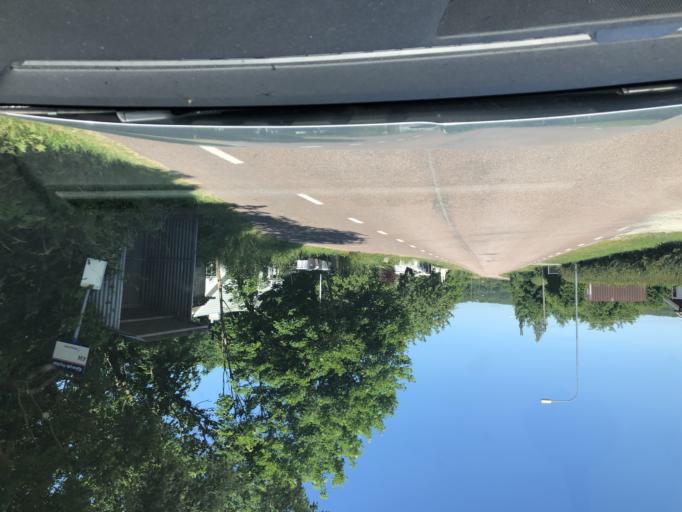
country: SE
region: Blekinge
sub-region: Solvesborgs Kommun
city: Soelvesborg
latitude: 56.1519
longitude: 14.6032
